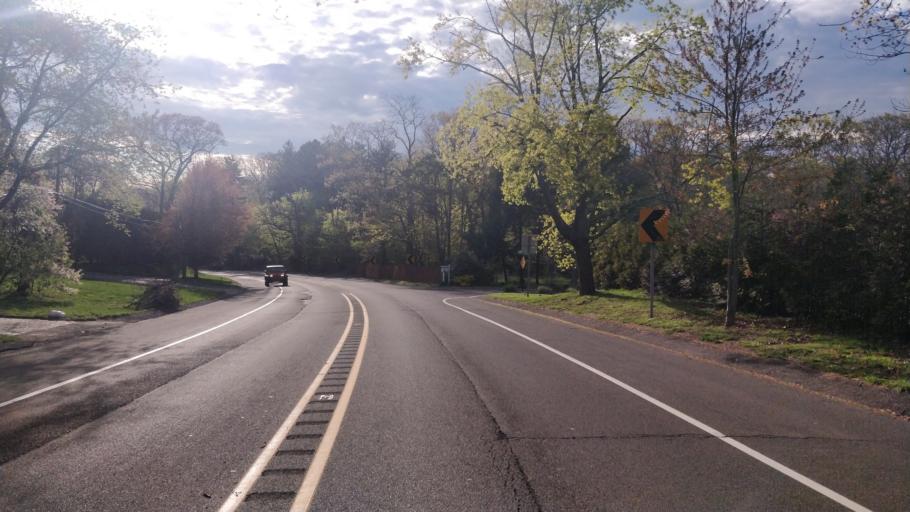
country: US
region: New York
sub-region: Suffolk County
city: Fort Salonga
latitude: 40.9129
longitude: -73.2880
